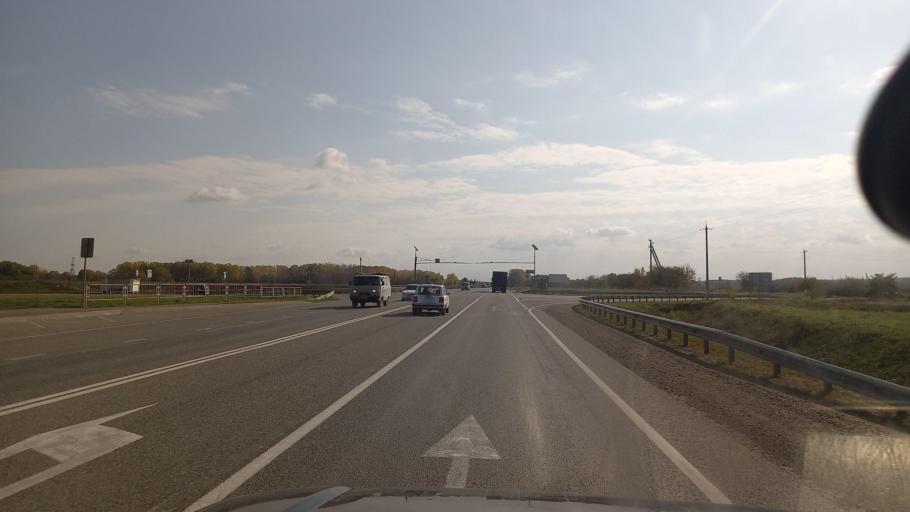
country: RU
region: Krasnodarskiy
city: Novoukrainskiy
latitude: 44.8897
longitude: 38.0742
